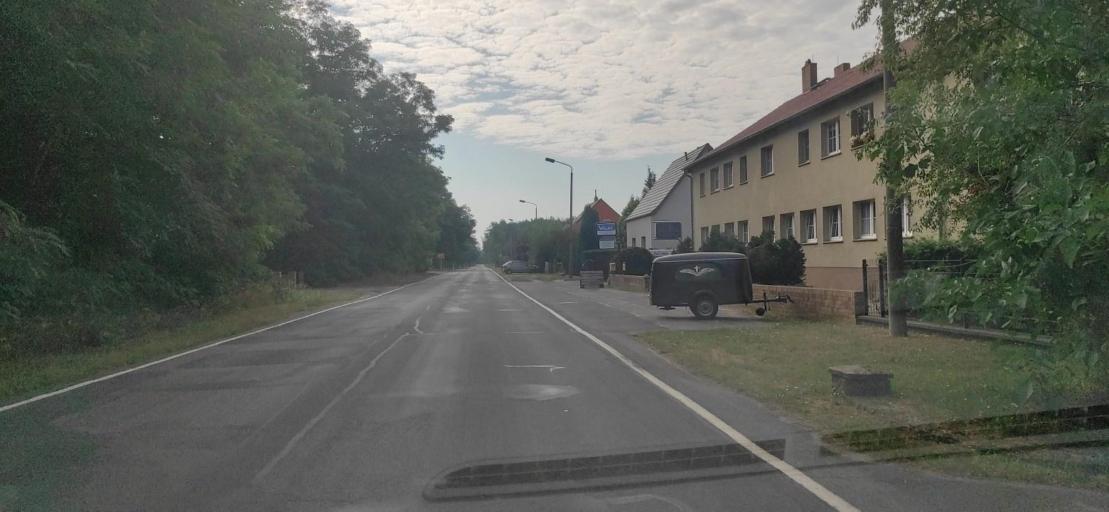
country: DE
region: Brandenburg
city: Forst
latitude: 51.7157
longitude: 14.6657
